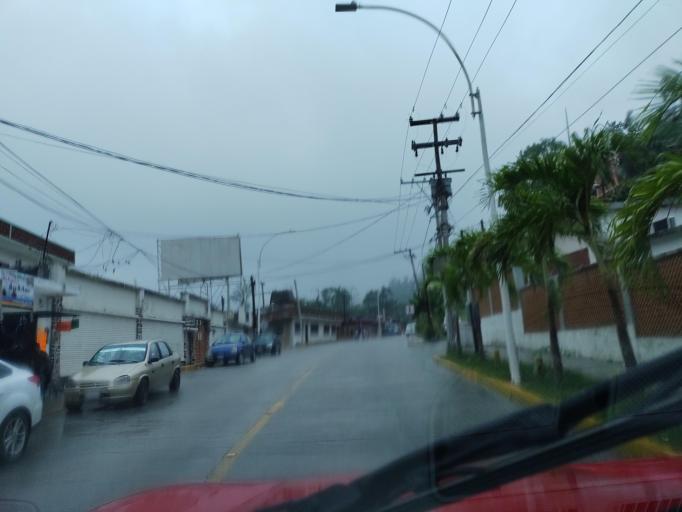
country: MX
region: Veracruz
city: Papantla de Olarte
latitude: 20.4502
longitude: -97.3293
